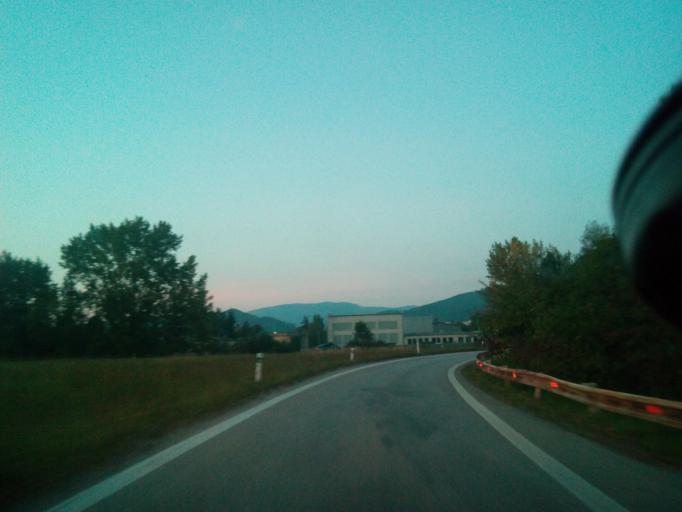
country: SK
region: Kosicky
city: Roznava
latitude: 48.6413
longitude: 20.5279
